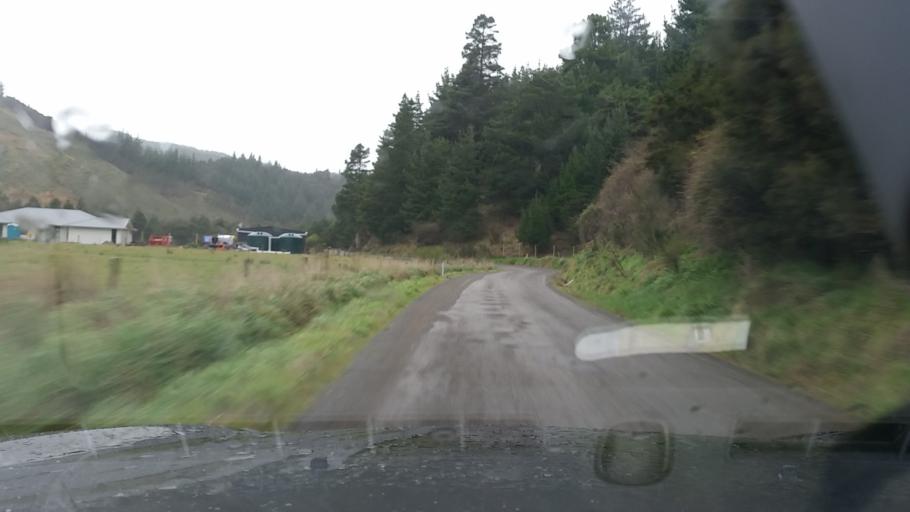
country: NZ
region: Marlborough
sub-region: Marlborough District
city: Blenheim
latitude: -41.4218
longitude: 173.8895
